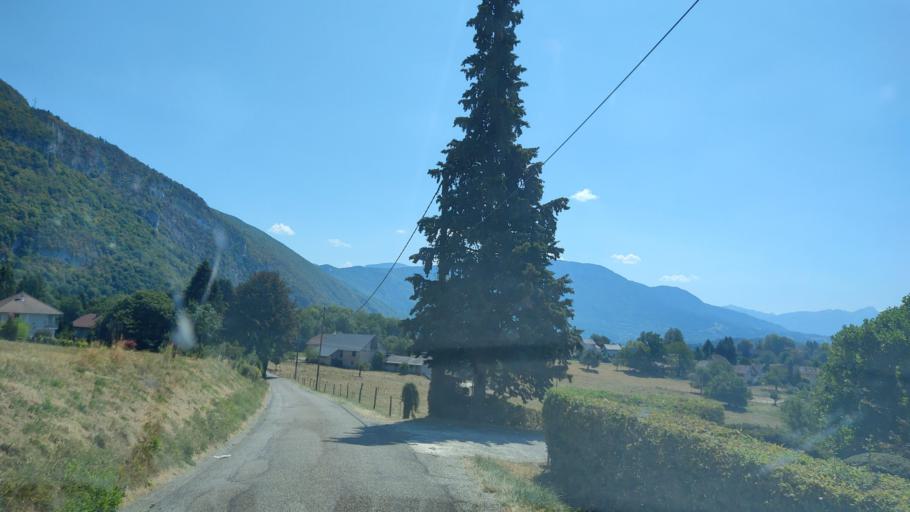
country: FR
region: Rhone-Alpes
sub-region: Departement de la Savoie
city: Novalaise
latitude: 45.5973
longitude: 5.7916
